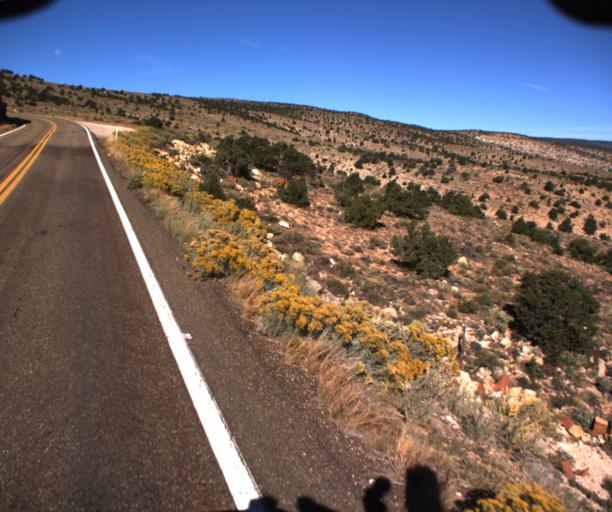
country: US
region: Arizona
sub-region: Coconino County
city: Fredonia
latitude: 36.7263
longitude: -112.0660
